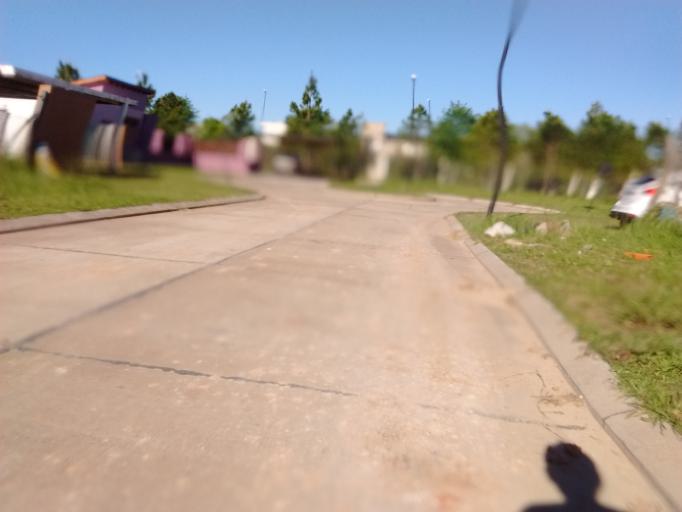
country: AR
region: Santa Fe
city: Funes
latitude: -32.9257
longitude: -60.8438
